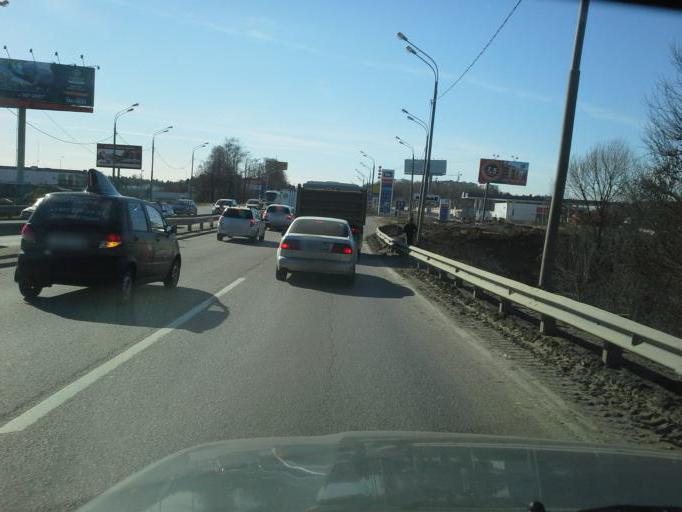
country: RU
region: Moscow
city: Novo-Peredelkino
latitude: 55.6724
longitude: 37.3142
